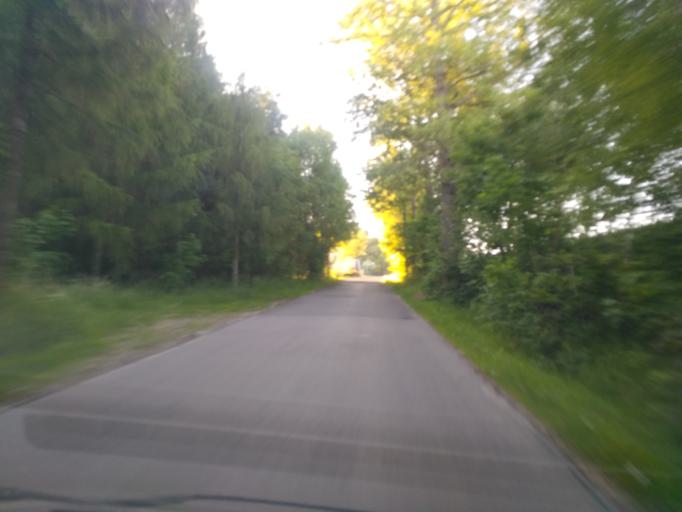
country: PL
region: Subcarpathian Voivodeship
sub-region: Powiat strzyzowski
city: Polomia
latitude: 49.8936
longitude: 21.8485
